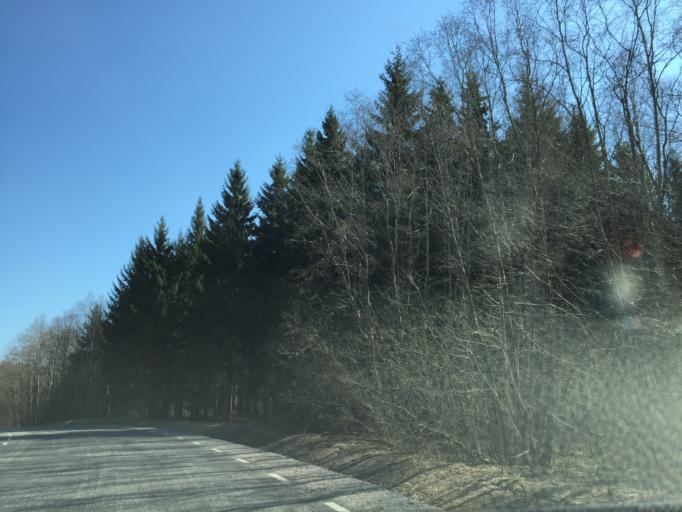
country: EE
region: Tartu
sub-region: Alatskivi vald
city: Kallaste
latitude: 58.5985
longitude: 27.0947
